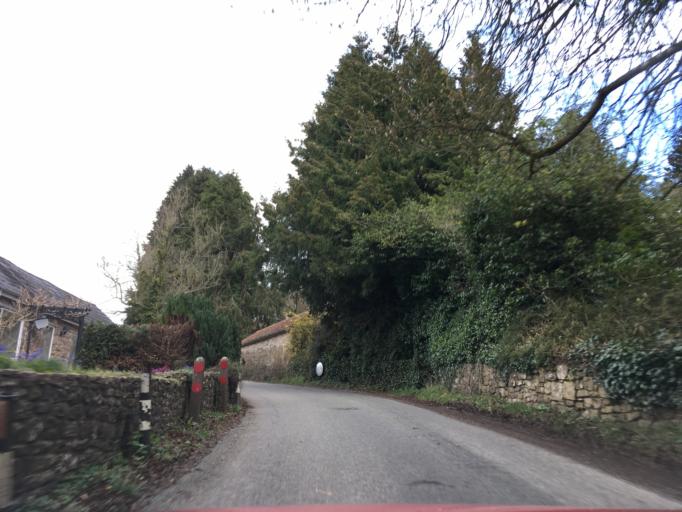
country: GB
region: England
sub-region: Gloucestershire
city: Coleford
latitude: 51.7475
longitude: -2.6466
